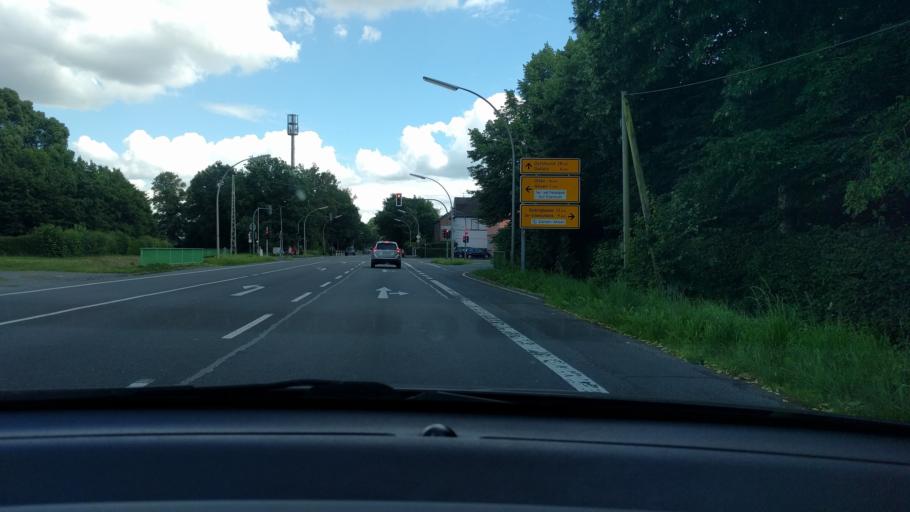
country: DE
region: North Rhine-Westphalia
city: Oer-Erkenschwick
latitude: 51.6988
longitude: 7.3075
